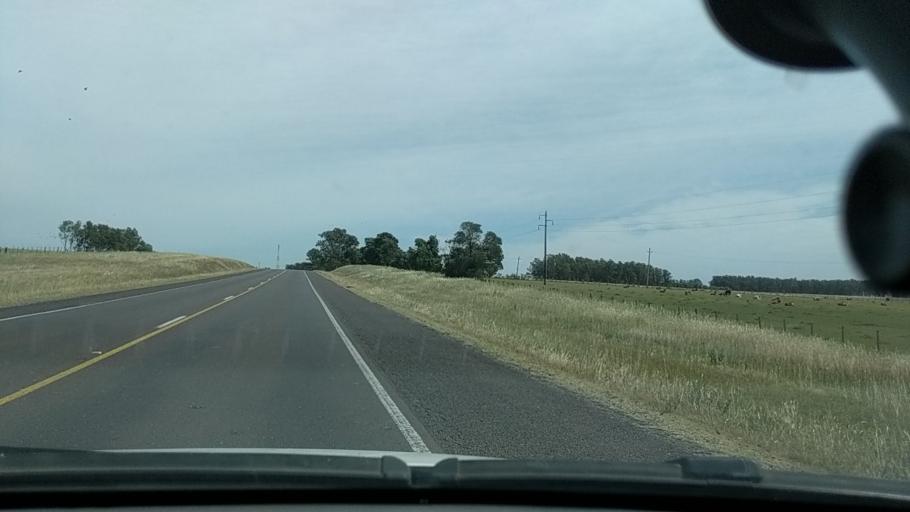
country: UY
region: Durazno
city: Durazno
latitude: -33.5091
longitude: -56.4156
